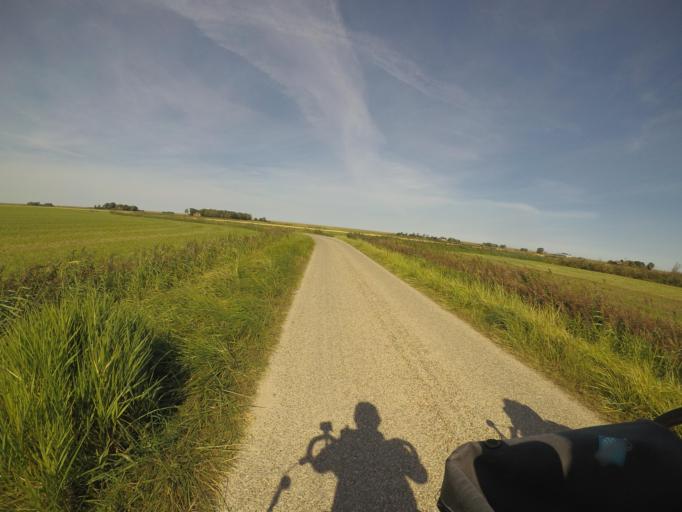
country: NL
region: Friesland
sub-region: Gemeente Ferwerderadiel
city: Ferwert
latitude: 53.3398
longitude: 5.8159
